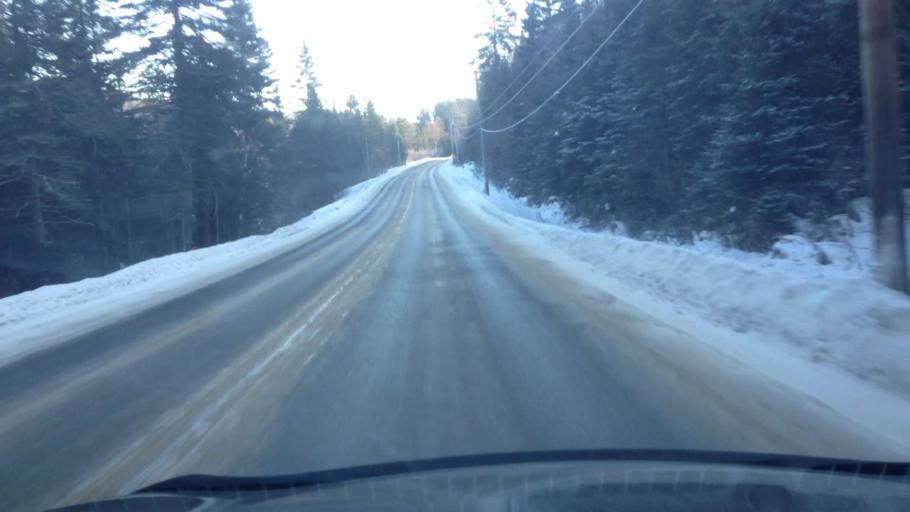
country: CA
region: Quebec
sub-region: Laurentides
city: Sainte-Agathe-des-Monts
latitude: 45.9206
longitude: -74.3854
